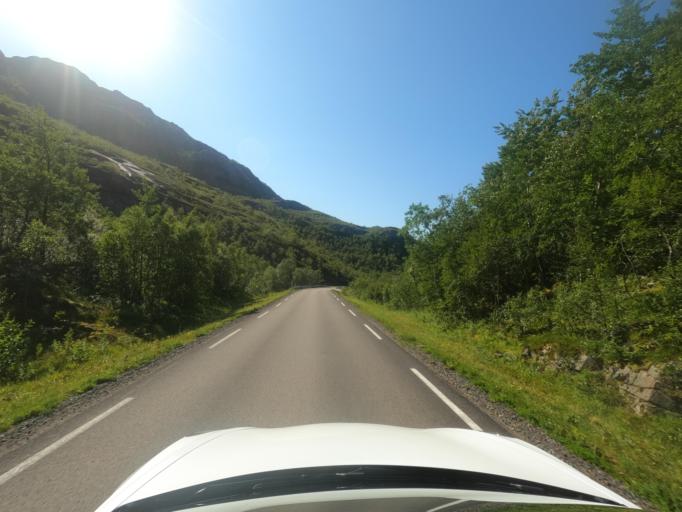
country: NO
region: Nordland
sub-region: Hadsel
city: Stokmarknes
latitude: 68.3294
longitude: 15.0155
